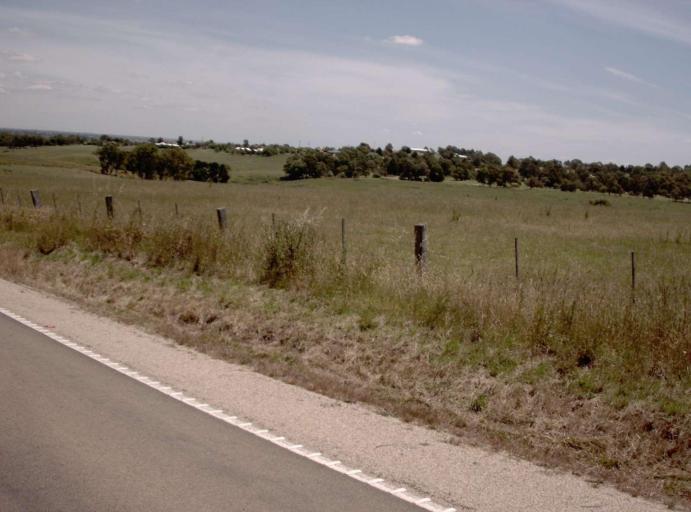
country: AU
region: Victoria
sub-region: East Gippsland
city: Bairnsdale
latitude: -37.8020
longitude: 147.6559
